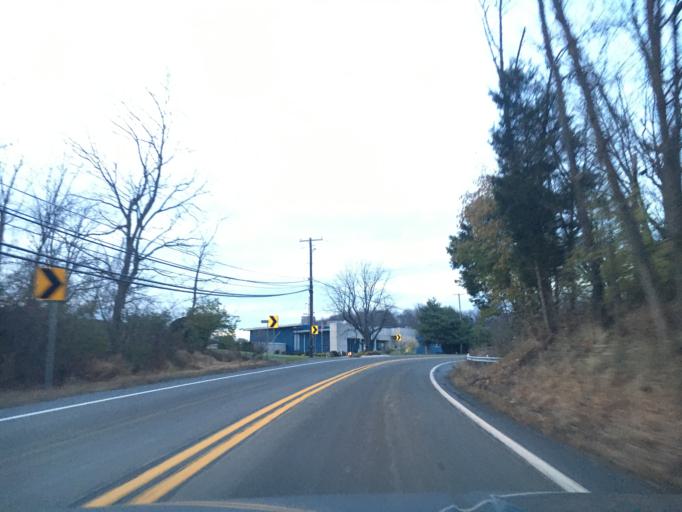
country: US
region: Pennsylvania
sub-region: Lehigh County
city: Egypt
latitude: 40.6709
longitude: -75.5680
